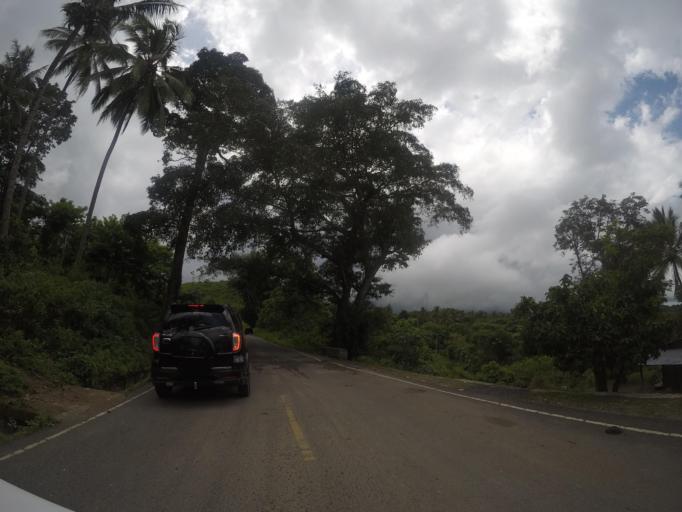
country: TL
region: Bobonaro
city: Maliana
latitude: -8.9656
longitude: 125.0521
